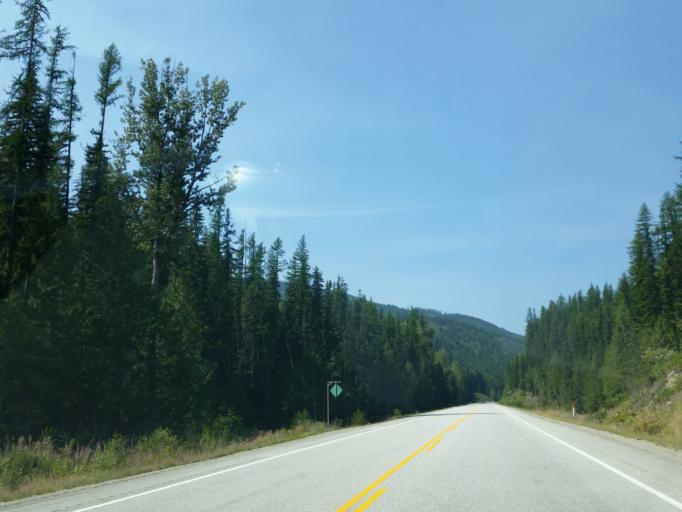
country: CA
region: British Columbia
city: Castlegar
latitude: 49.2981
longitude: -117.8057
